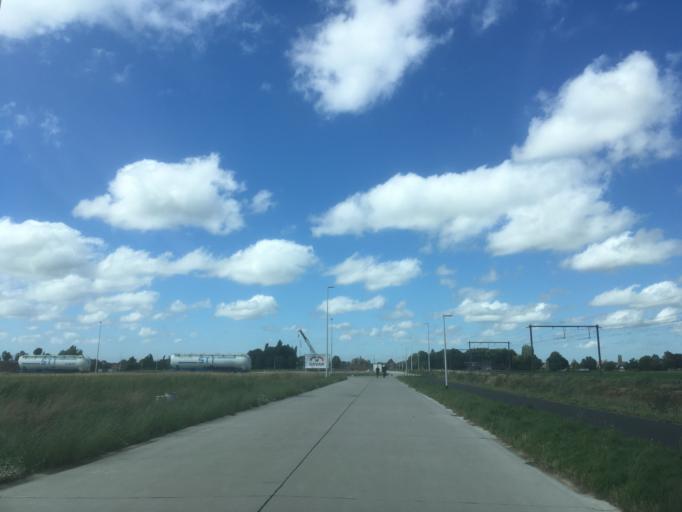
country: BE
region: Flanders
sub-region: Provincie West-Vlaanderen
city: Torhout
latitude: 51.0483
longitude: 3.1102
